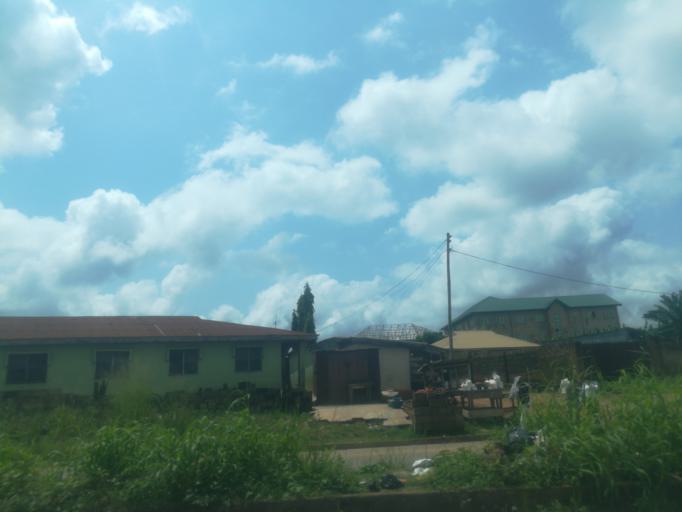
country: NG
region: Oyo
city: Ibadan
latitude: 7.3630
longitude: 3.8238
